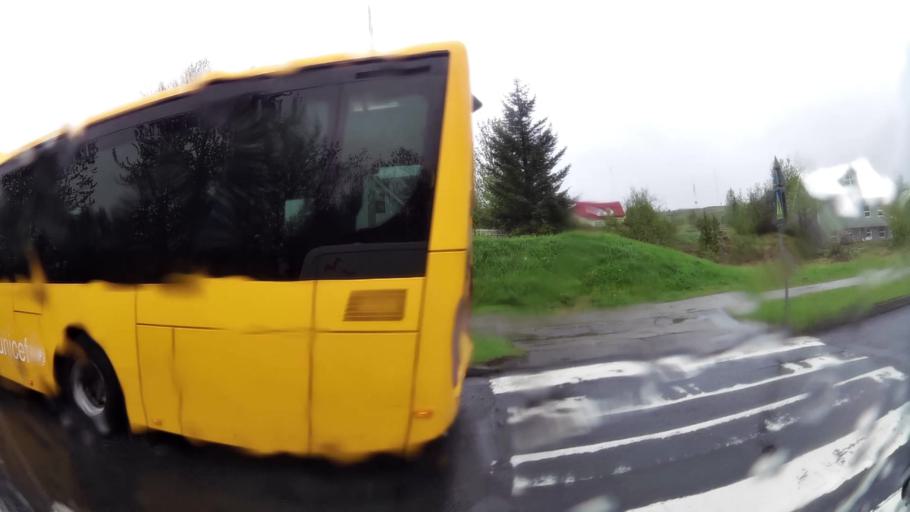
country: IS
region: Capital Region
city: Reykjavik
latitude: 64.0958
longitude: -21.8283
